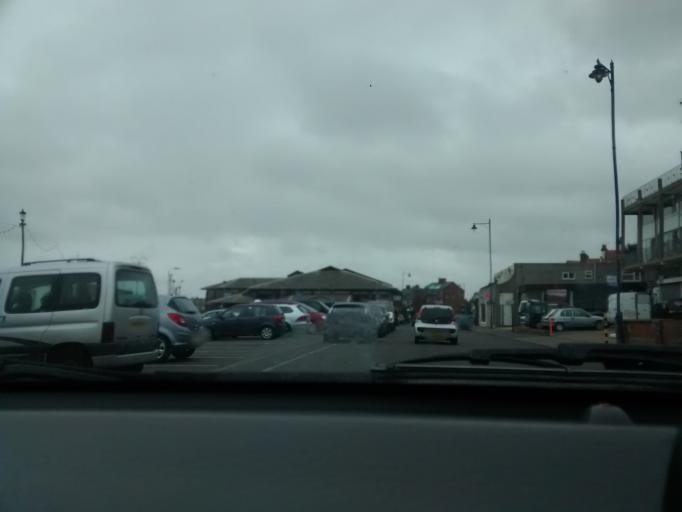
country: GB
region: England
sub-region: Suffolk
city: Felixstowe
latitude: 51.9589
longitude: 1.3475
